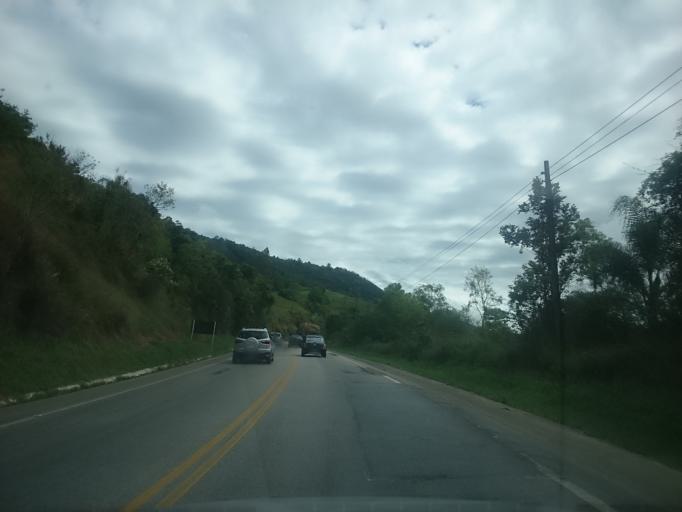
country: BR
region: Santa Catarina
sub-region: Anitapolis
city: Anitapolis
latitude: -27.6934
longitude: -49.3085
